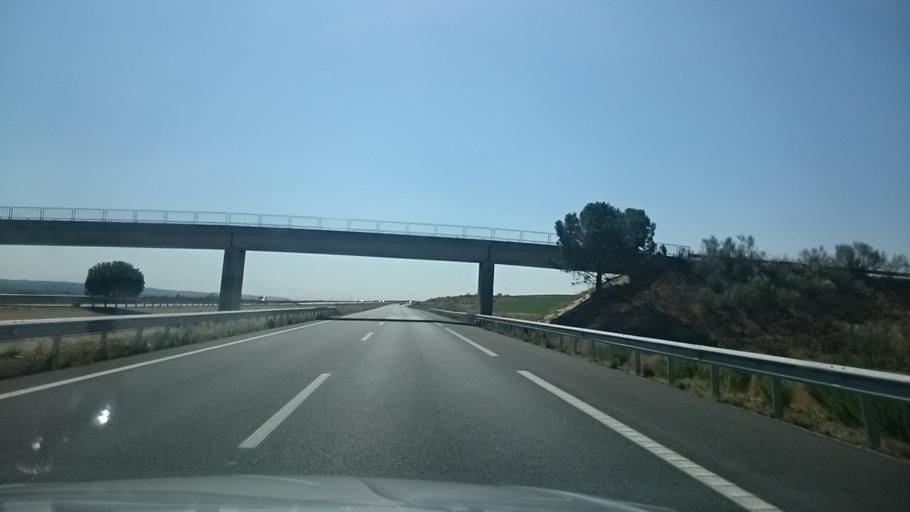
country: ES
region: Aragon
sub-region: Provincia de Zaragoza
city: Boquineni
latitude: 41.8171
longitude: -1.2807
